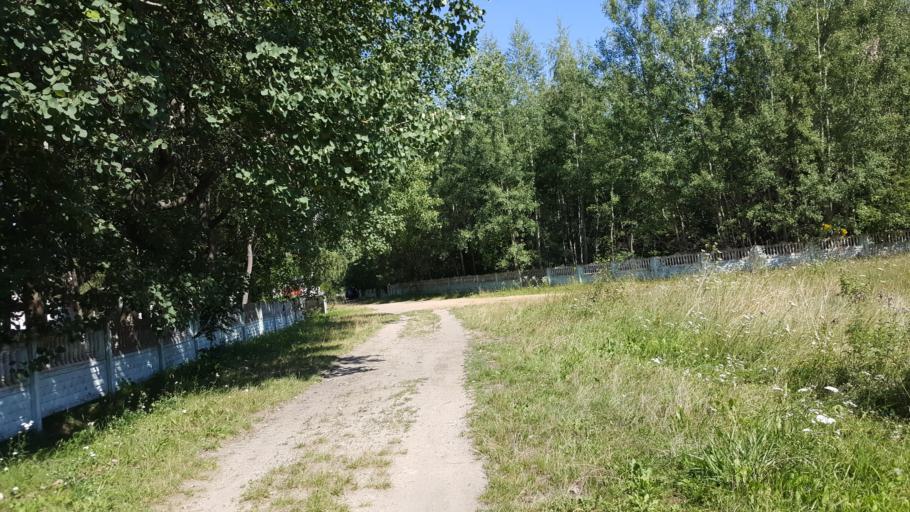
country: BY
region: Brest
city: Charnawchytsy
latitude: 52.2549
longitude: 23.5831
